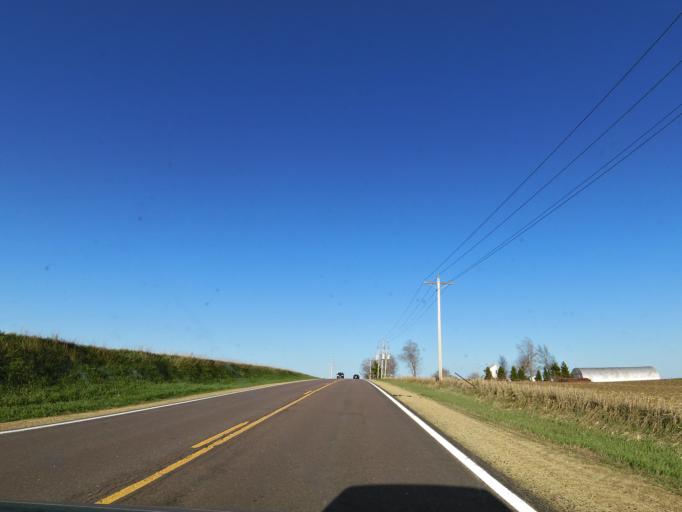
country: US
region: Minnesota
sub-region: Goodhue County
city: Cannon Falls
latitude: 44.6012
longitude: -92.9092
